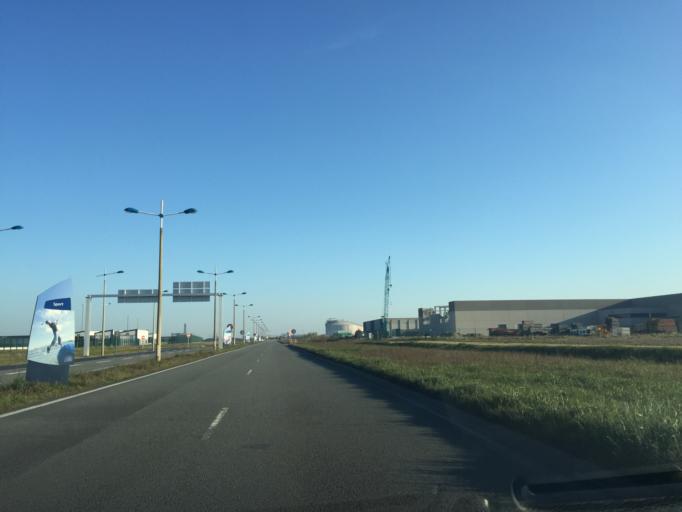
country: FR
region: Nord-Pas-de-Calais
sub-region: Departement du Nord
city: Loon-Plage
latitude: 51.0159
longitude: 2.2005
